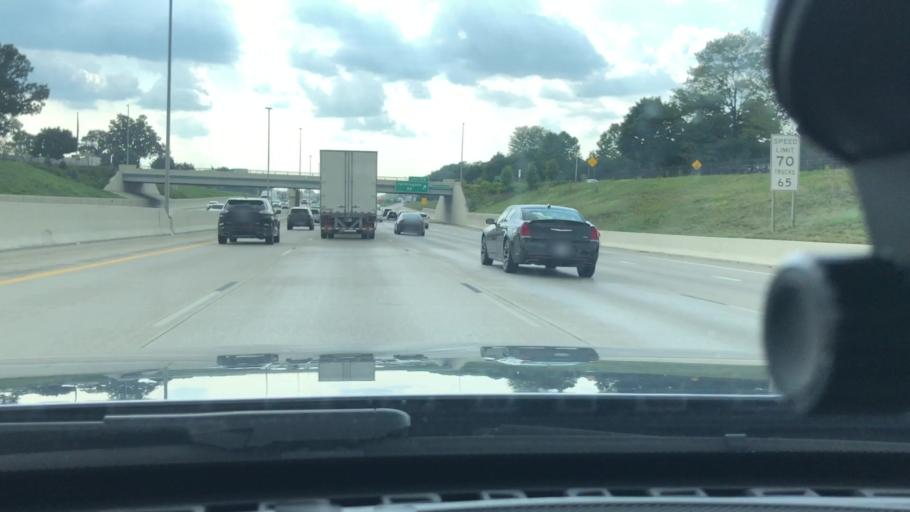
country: US
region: Michigan
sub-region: Wayne County
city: Livonia
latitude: 42.3829
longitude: -83.3639
